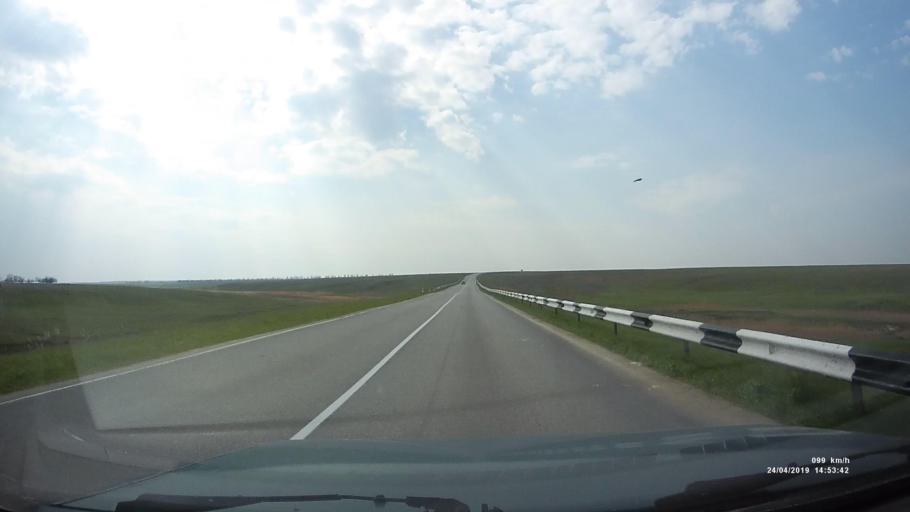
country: RU
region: Rostov
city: Remontnoye
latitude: 46.5314
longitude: 43.6558
